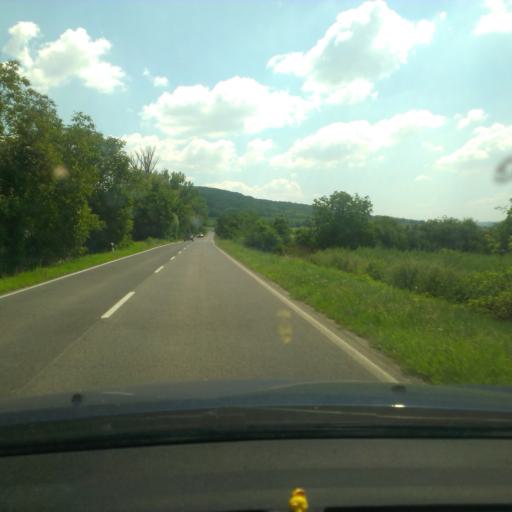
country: SK
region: Trnavsky
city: Hlohovec
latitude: 48.4674
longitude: 17.8124
